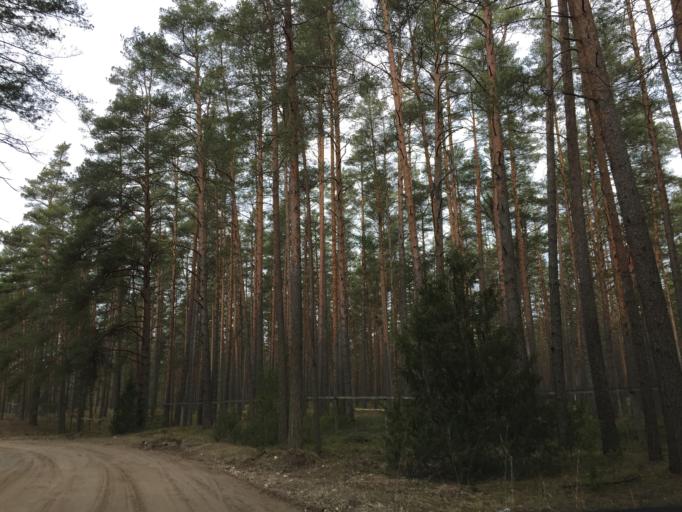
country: LV
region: Garkalne
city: Garkalne
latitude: 57.0688
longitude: 24.4655
